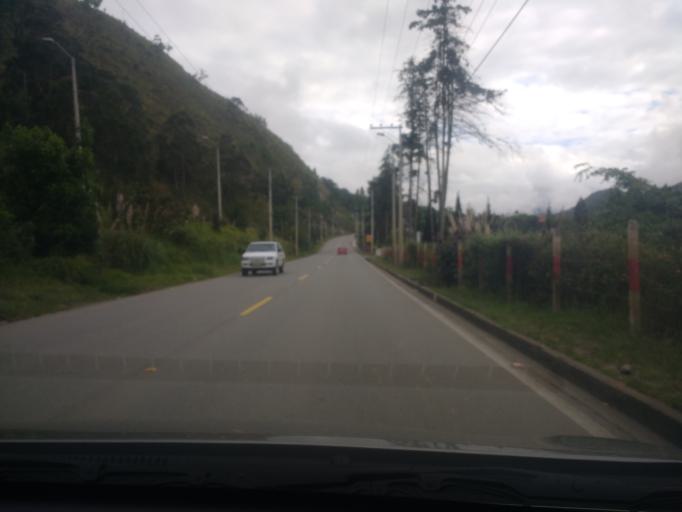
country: EC
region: Azuay
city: La Union
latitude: -2.8410
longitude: -78.7731
